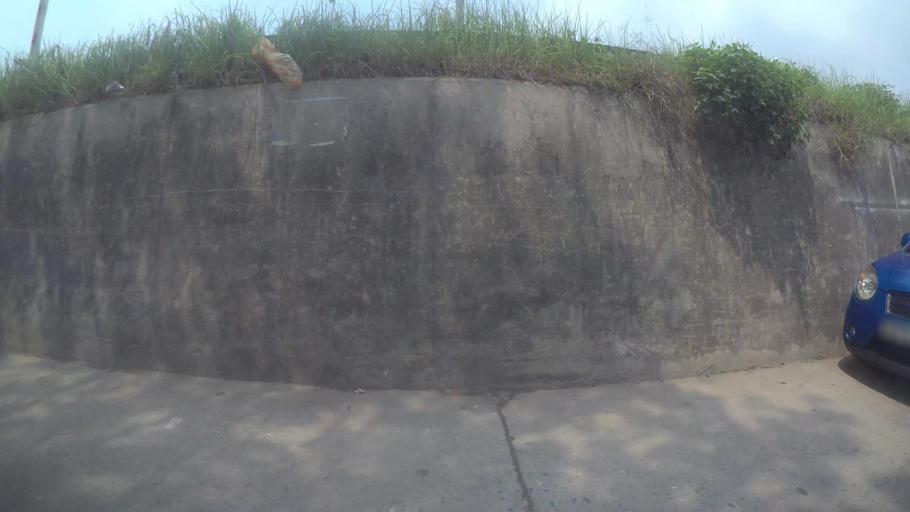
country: VN
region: Ha Noi
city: Tay Ho
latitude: 21.0897
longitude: 105.8081
